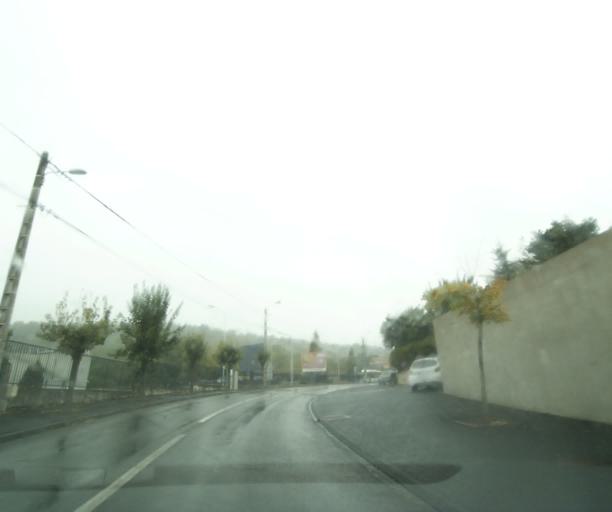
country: FR
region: Auvergne
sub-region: Departement du Puy-de-Dome
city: Cebazat
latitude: 45.8388
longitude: 3.0926
